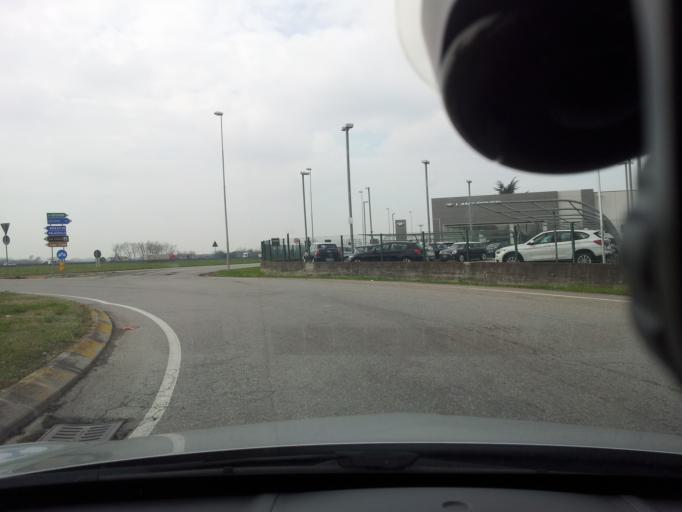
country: IT
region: Lombardy
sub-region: Provincia di Bergamo
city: Grumello del Monte
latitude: 45.6299
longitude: 9.8796
